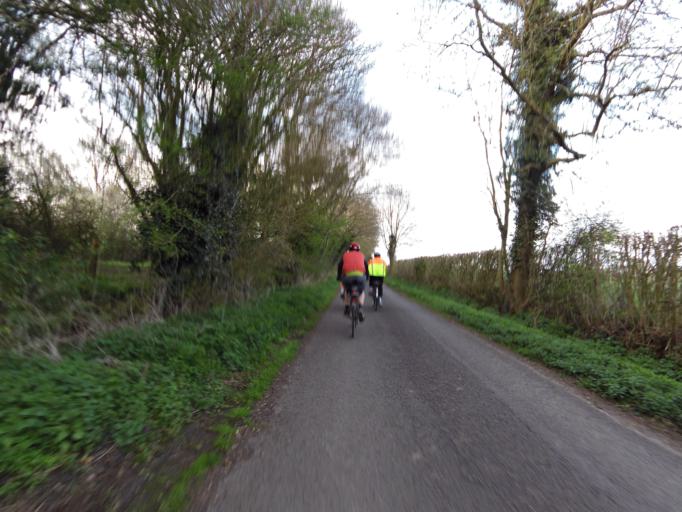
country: GB
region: England
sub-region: Suffolk
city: Debenham
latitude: 52.1467
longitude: 1.2049
